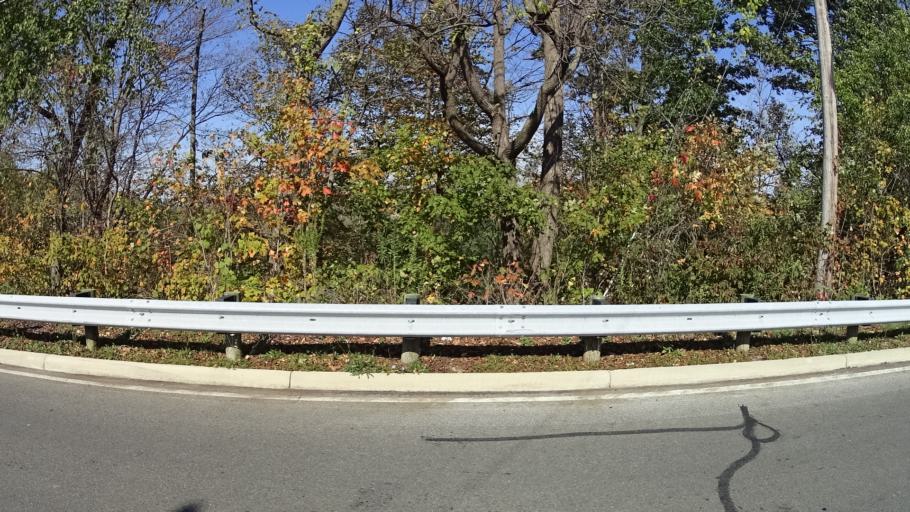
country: US
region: Ohio
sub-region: Lorain County
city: Vermilion
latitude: 41.4133
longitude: -82.3493
